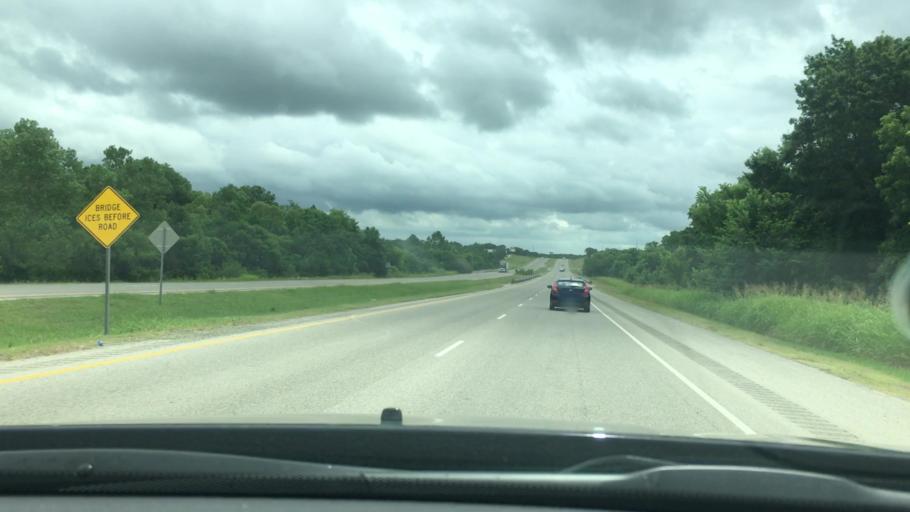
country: US
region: Oklahoma
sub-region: Carter County
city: Ardmore
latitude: 34.1353
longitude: -97.1065
